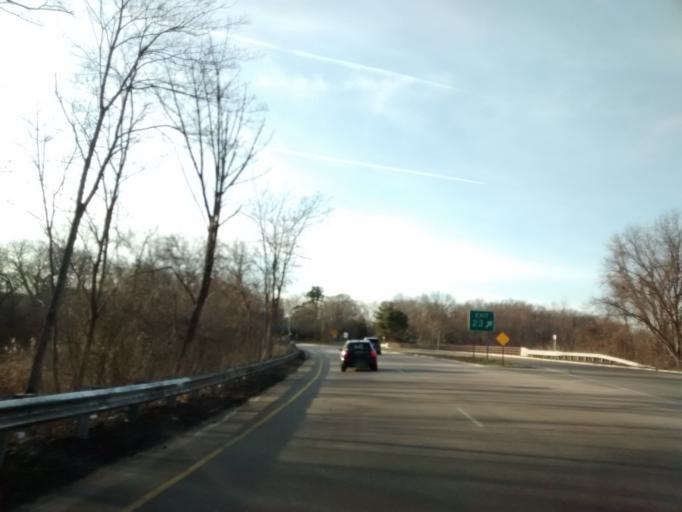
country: US
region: Massachusetts
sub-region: Middlesex County
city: Waltham
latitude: 42.3367
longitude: -71.2567
